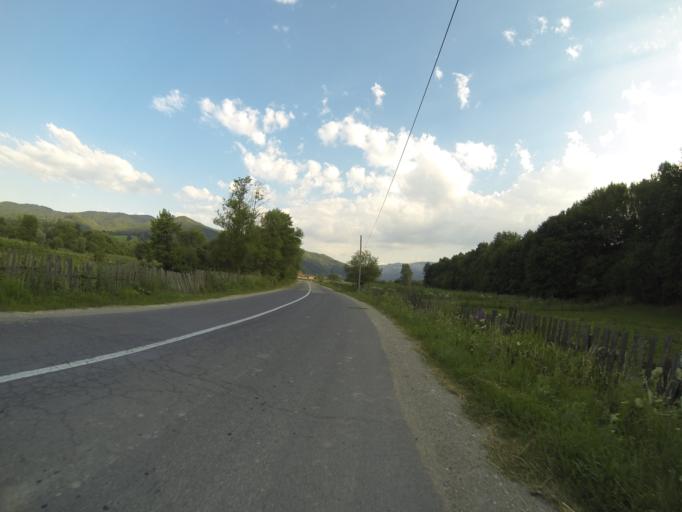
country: RO
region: Brasov
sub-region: Comuna Sinca Noua
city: Sinca Noua
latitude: 45.7128
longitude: 25.2421
